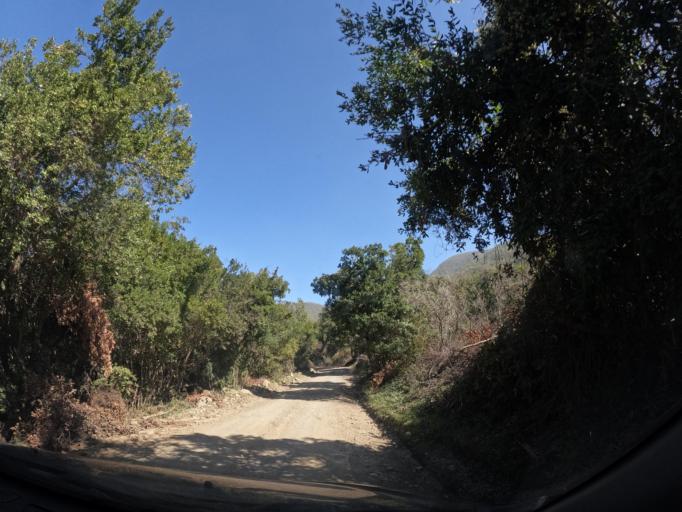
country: CL
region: Maule
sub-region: Provincia de Linares
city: Longavi
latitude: -36.2777
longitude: -71.4157
